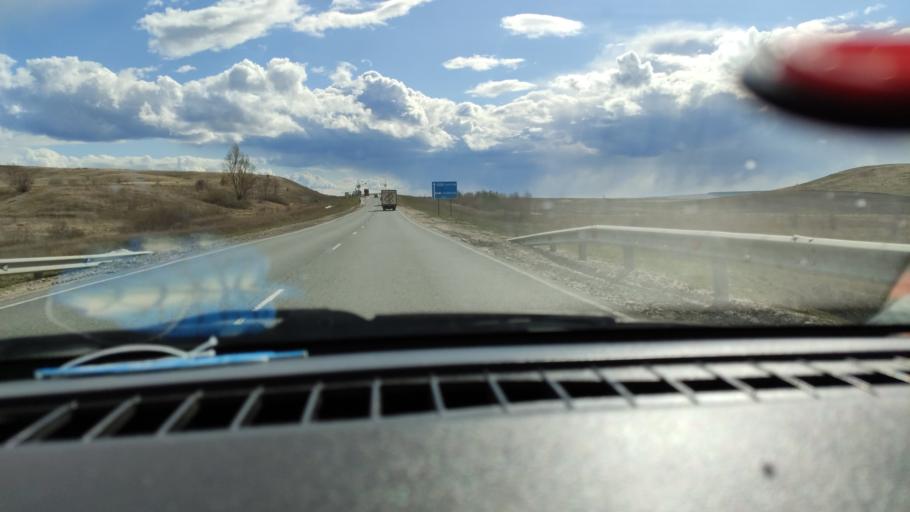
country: RU
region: Saratov
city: Alekseyevka
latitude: 52.3473
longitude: 47.9379
